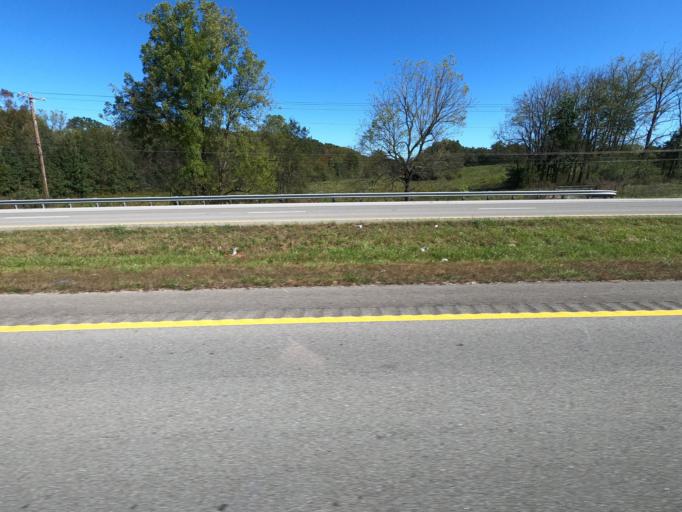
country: US
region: Tennessee
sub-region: Lawrence County
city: Lawrenceburg
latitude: 35.3891
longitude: -87.2762
